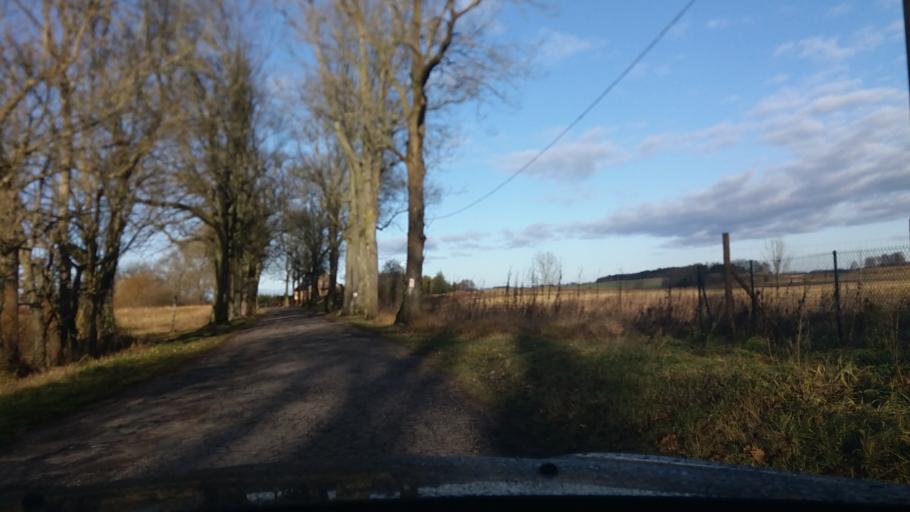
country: PL
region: West Pomeranian Voivodeship
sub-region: Powiat choszczenski
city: Drawno
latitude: 53.1802
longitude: 15.8039
